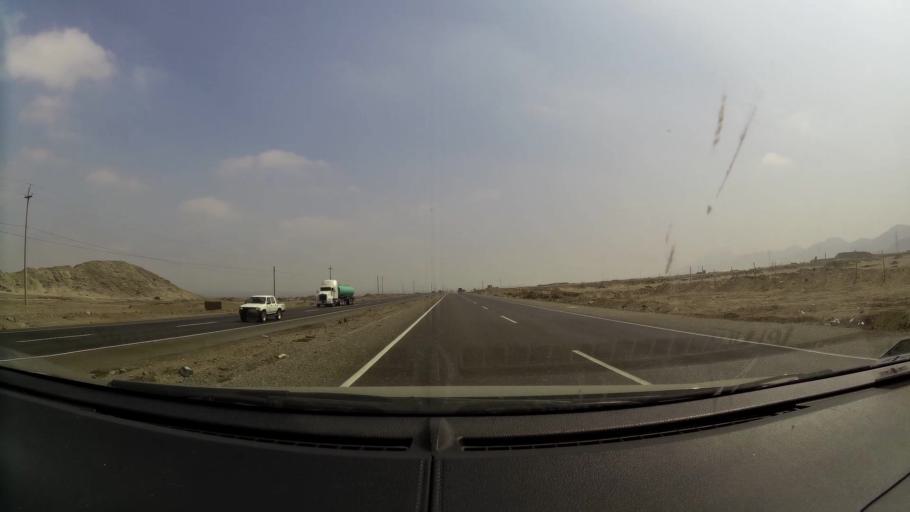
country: PE
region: La Libertad
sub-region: Ascope
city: Chicama
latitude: -7.9096
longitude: -79.1158
